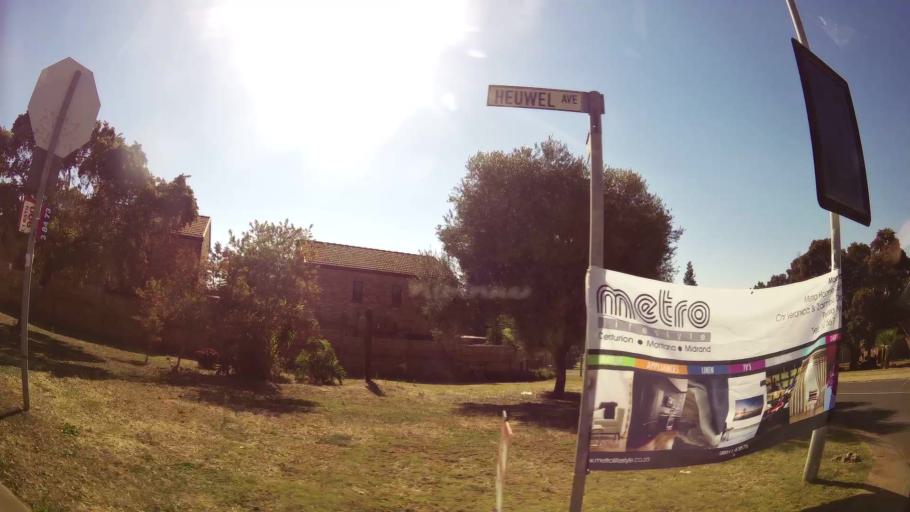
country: ZA
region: Gauteng
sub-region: City of Tshwane Metropolitan Municipality
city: Centurion
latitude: -25.8535
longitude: 28.1805
